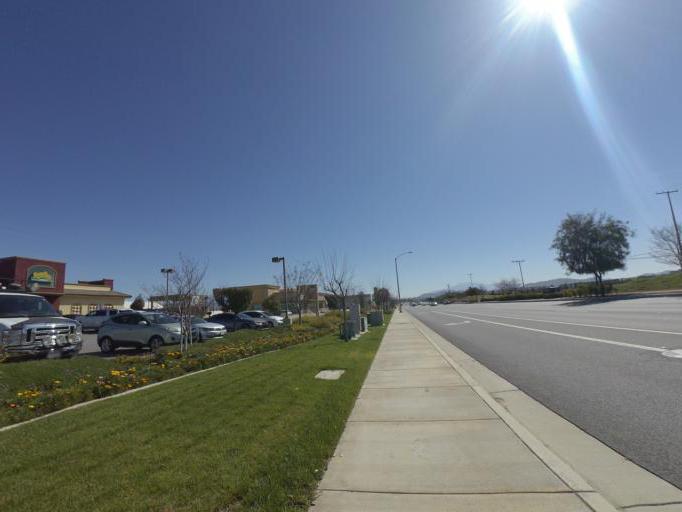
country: US
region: California
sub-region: Riverside County
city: March Air Force Base
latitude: 33.9169
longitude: -117.2961
